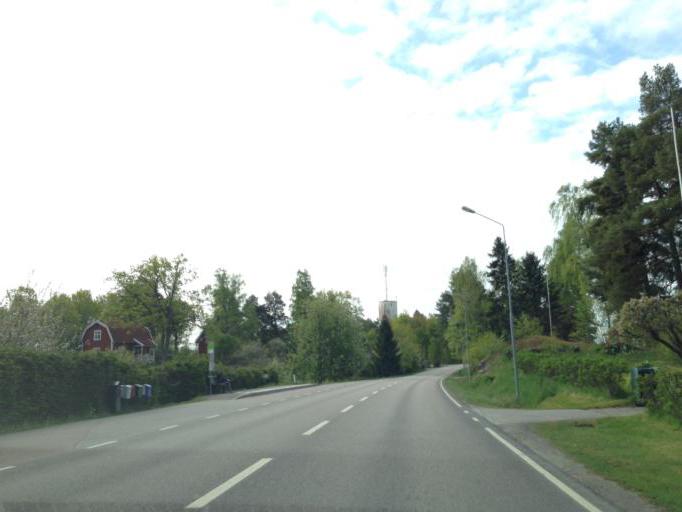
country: SE
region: Soedermanland
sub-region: Flens Kommun
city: Malmkoping
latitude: 59.0735
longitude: 16.8165
